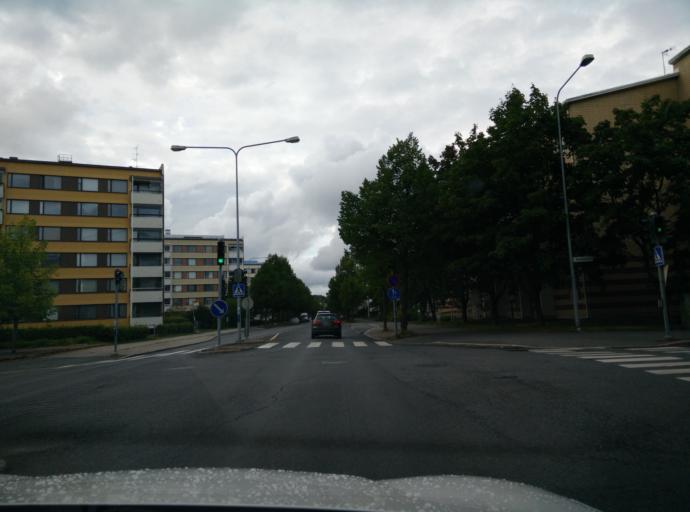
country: FI
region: Haeme
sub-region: Haemeenlinna
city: Haemeenlinna
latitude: 60.9968
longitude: 24.4418
